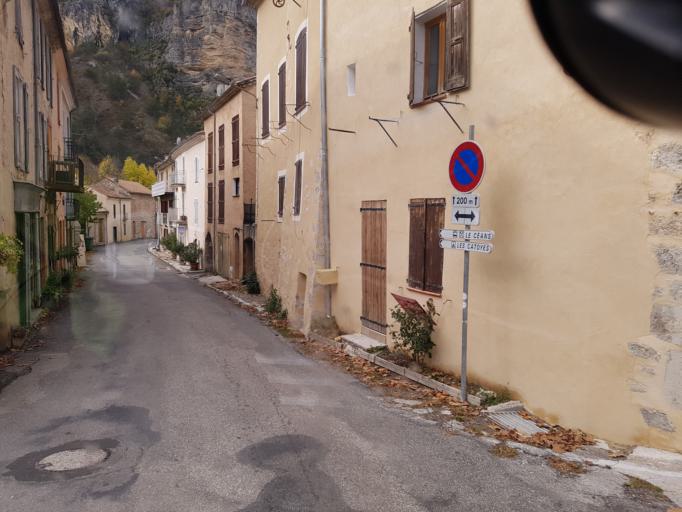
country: FR
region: Provence-Alpes-Cote d'Azur
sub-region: Departement des Hautes-Alpes
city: Serres
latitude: 44.3135
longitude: 5.6926
